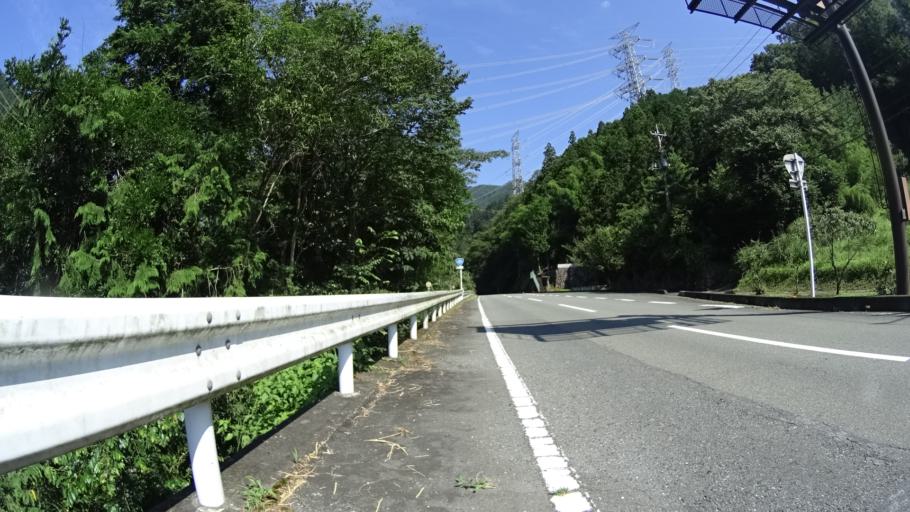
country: JP
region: Saitama
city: Chichibu
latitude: 36.0302
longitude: 138.9396
